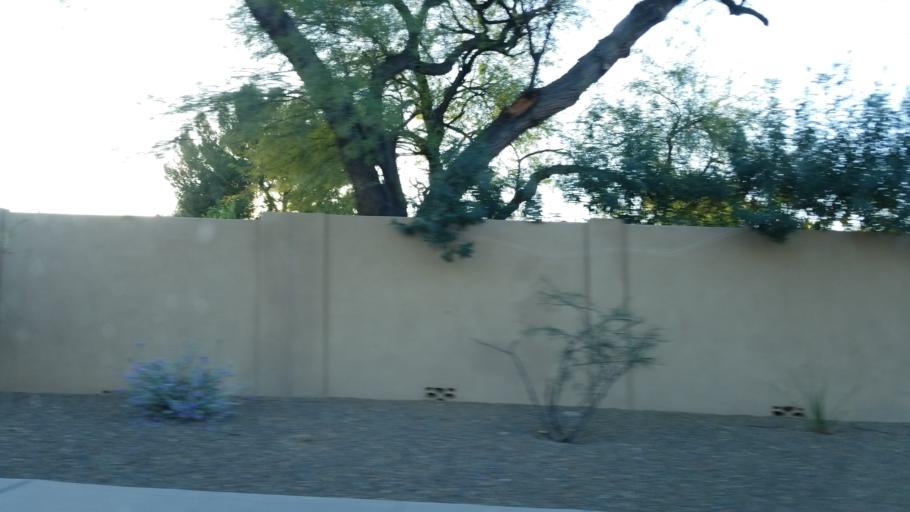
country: US
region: Arizona
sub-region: Maricopa County
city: Paradise Valley
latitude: 33.5798
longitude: -111.9174
